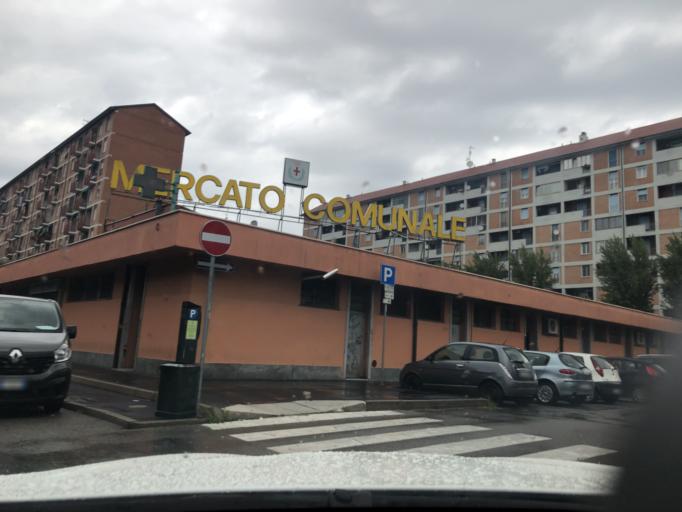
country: IT
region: Lombardy
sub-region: Citta metropolitana di Milano
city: Baranzate
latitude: 45.4906
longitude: 9.1219
